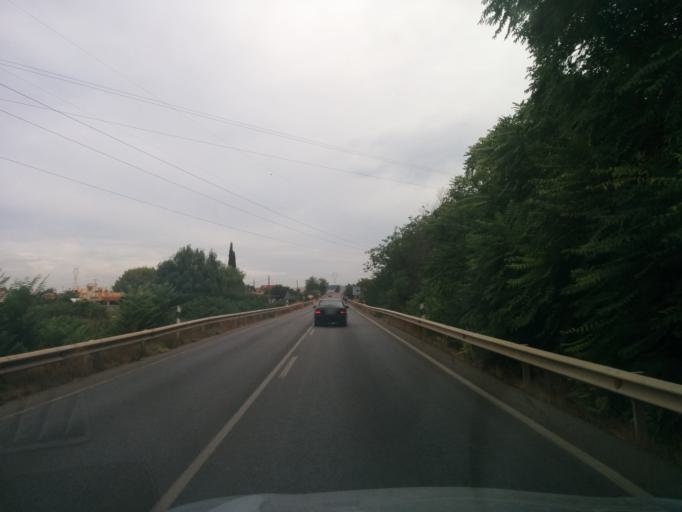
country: ES
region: Andalusia
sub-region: Provincia de Sevilla
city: La Algaba
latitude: 37.4924
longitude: -6.0103
